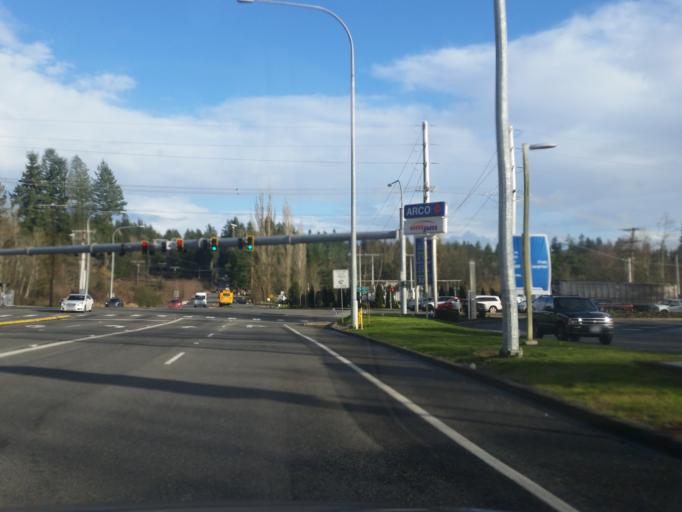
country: US
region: Washington
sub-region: Snohomish County
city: Maltby
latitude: 47.8048
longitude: -122.1445
